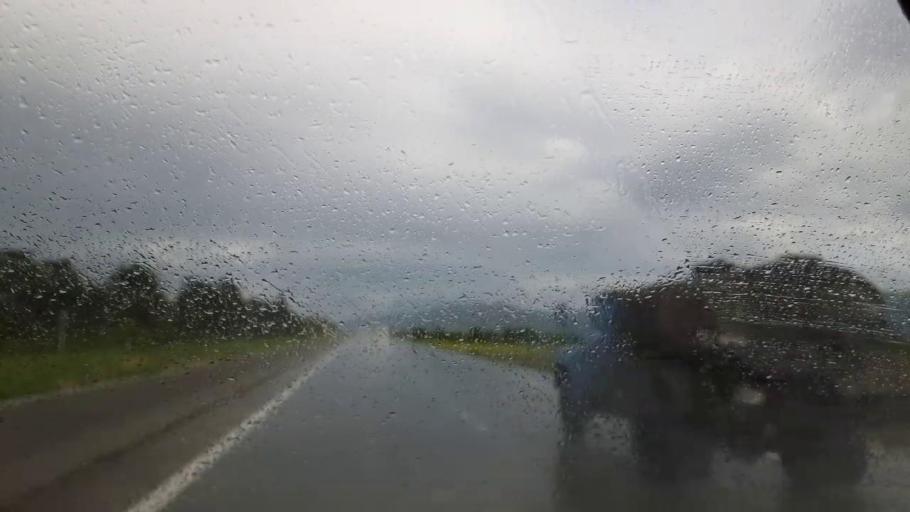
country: GE
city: Agara
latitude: 42.0407
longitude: 43.9298
